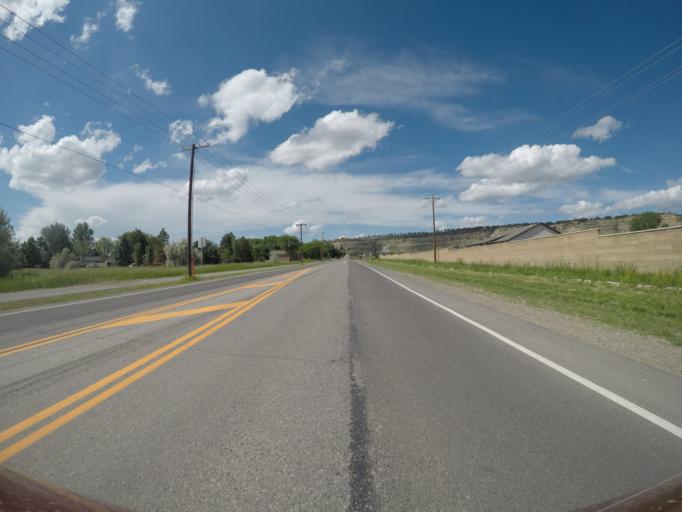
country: US
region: Montana
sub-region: Yellowstone County
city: Billings
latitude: 45.7974
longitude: -108.6526
